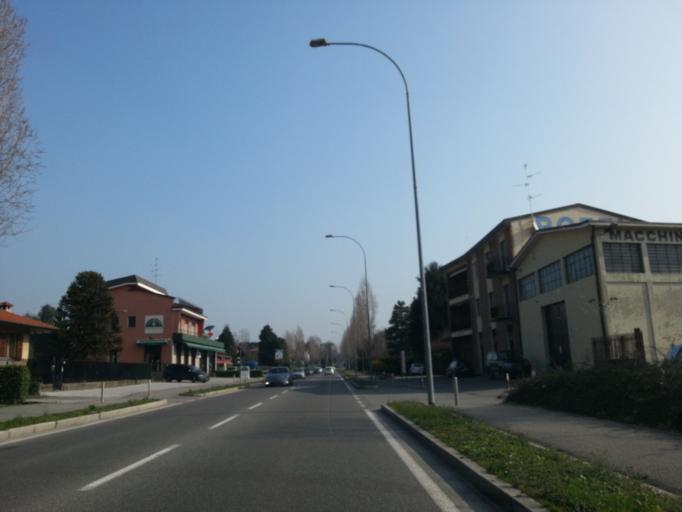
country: IT
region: Lombardy
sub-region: Provincia di Monza e Brianza
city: Carate Brianza
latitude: 45.6680
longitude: 9.2269
